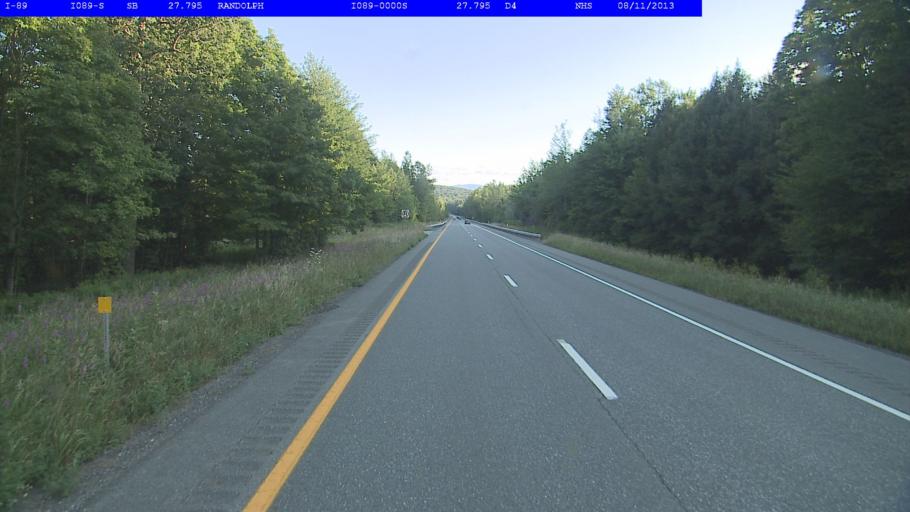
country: US
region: Vermont
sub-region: Orange County
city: Randolph
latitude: 43.9010
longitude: -72.6155
